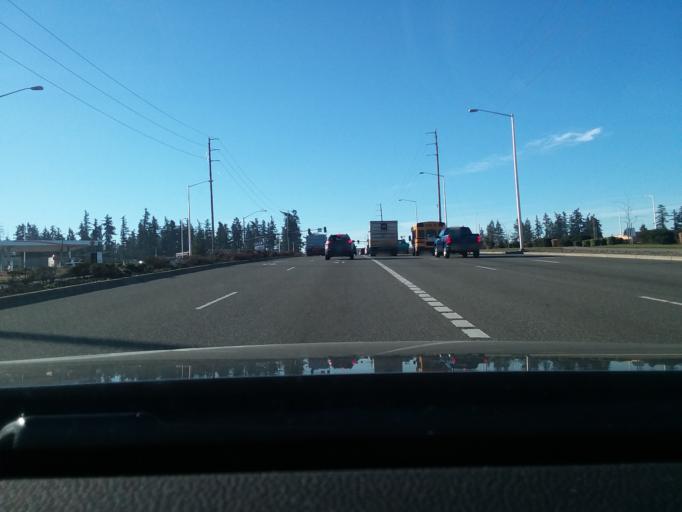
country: US
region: Washington
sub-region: Pierce County
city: Frederickson
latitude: 47.0978
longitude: -122.3566
